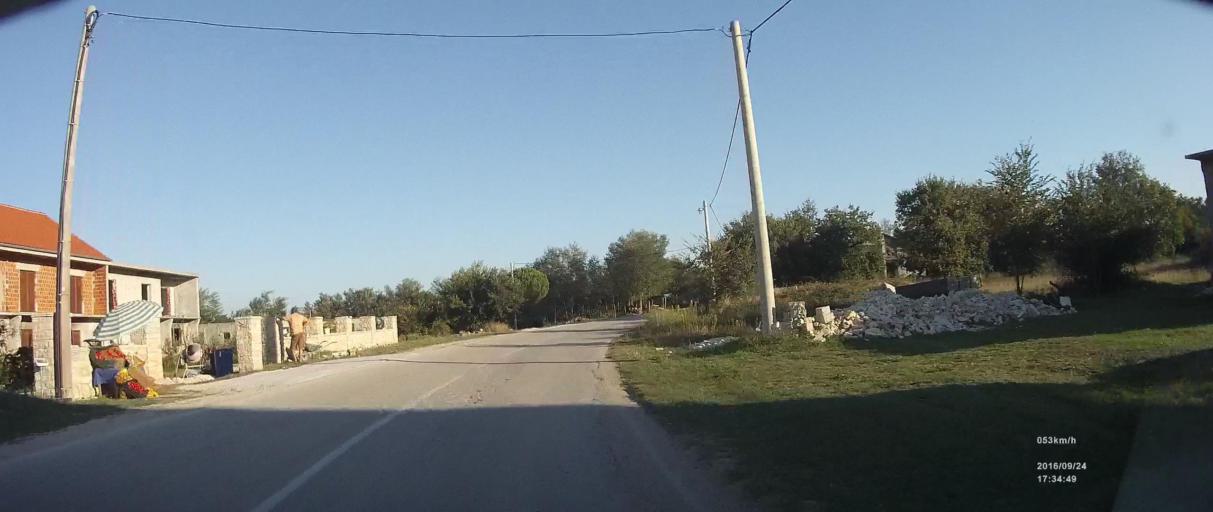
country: HR
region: Zadarska
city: Posedarje
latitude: 44.1652
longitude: 15.4636
